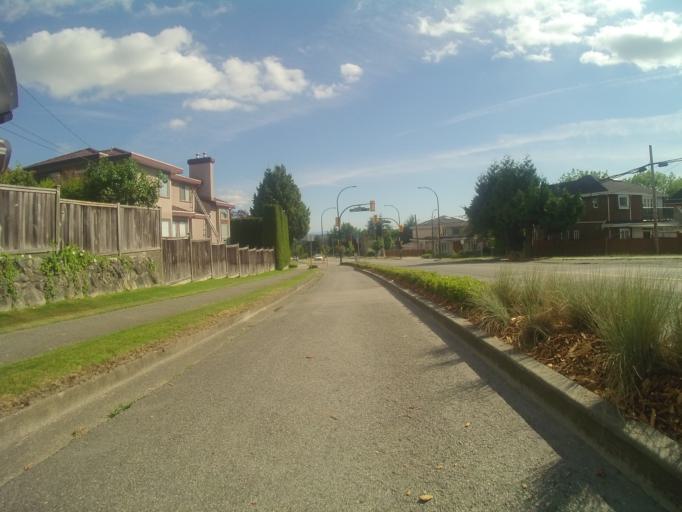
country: CA
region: British Columbia
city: Vancouver
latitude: 49.2167
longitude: -123.0718
